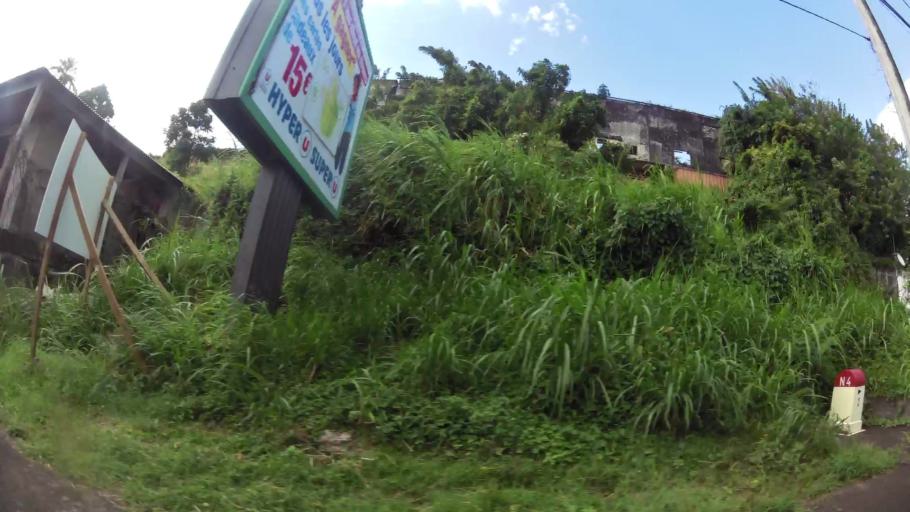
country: MQ
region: Martinique
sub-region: Martinique
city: Fort-de-France
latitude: 14.6206
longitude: -61.0605
